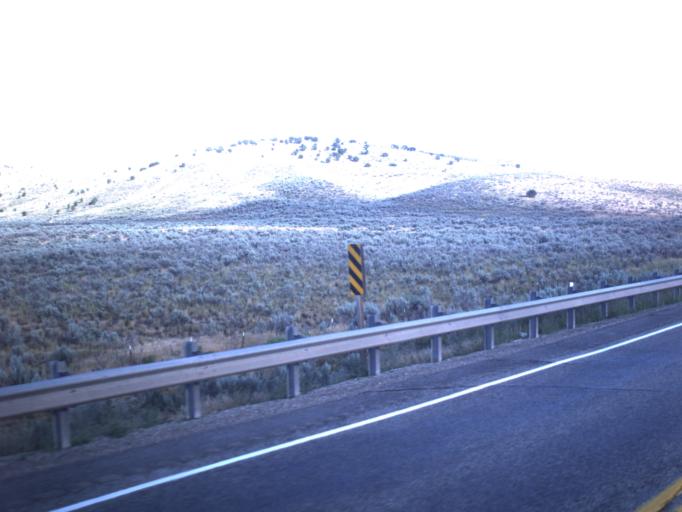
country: US
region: Utah
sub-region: Sanpete County
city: Fairview
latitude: 39.8338
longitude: -111.5120
